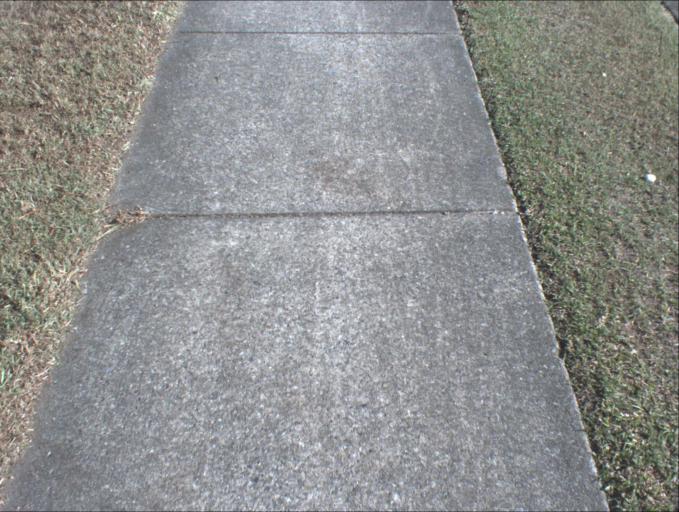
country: AU
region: Queensland
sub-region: Logan
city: Beenleigh
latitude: -27.7164
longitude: 153.1827
